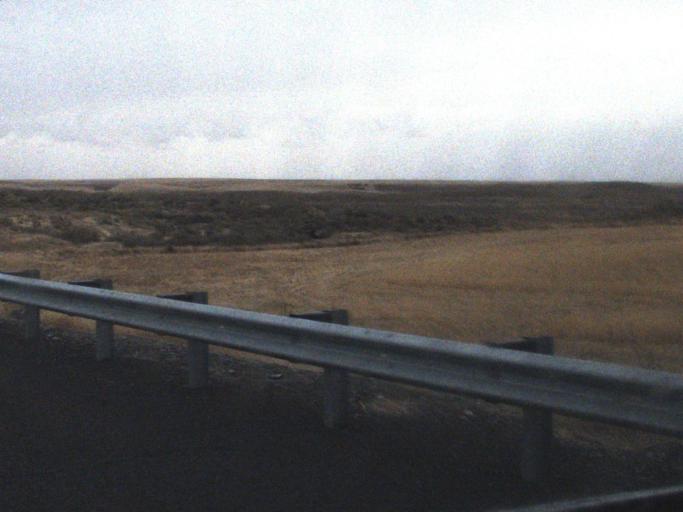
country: US
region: Washington
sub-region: Franklin County
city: Connell
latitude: 46.7951
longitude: -118.5269
